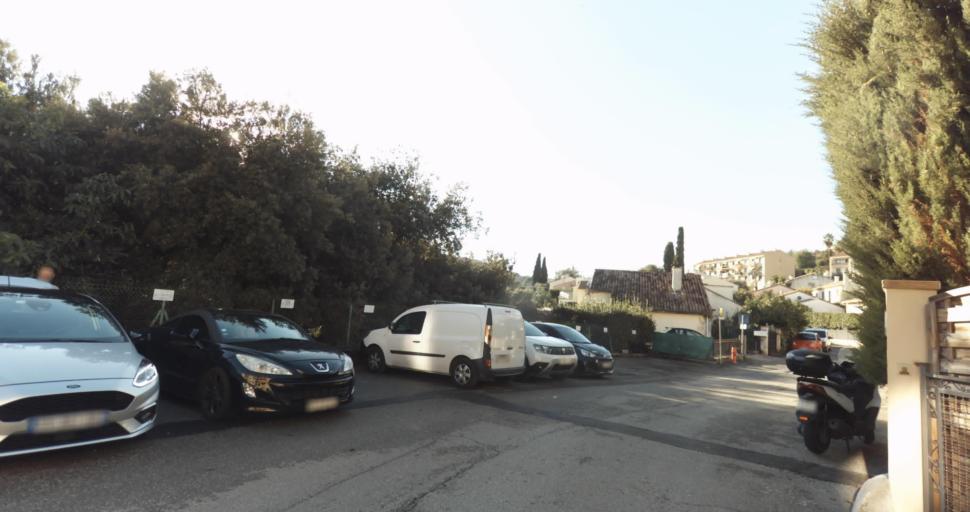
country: FR
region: Provence-Alpes-Cote d'Azur
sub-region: Departement des Alpes-Maritimes
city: Vence
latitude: 43.7255
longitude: 7.1232
